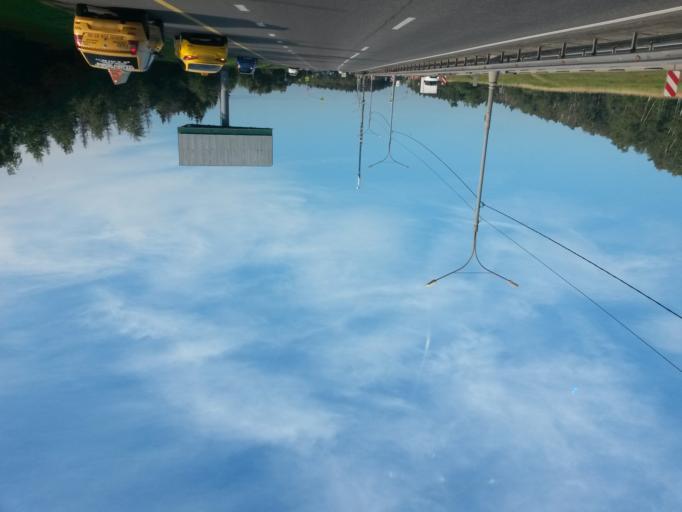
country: RU
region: Moskovskaya
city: Vostryakovo
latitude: 55.4560
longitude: 37.8556
